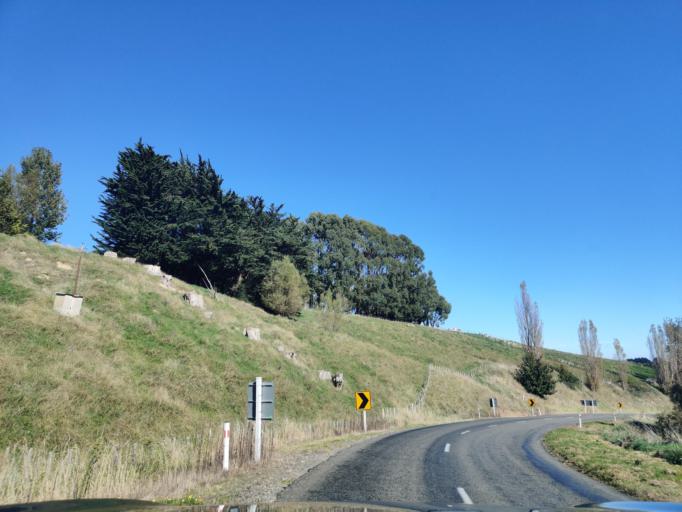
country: NZ
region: Manawatu-Wanganui
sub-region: Palmerston North City
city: Palmerston North
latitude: -40.2593
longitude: 175.7142
